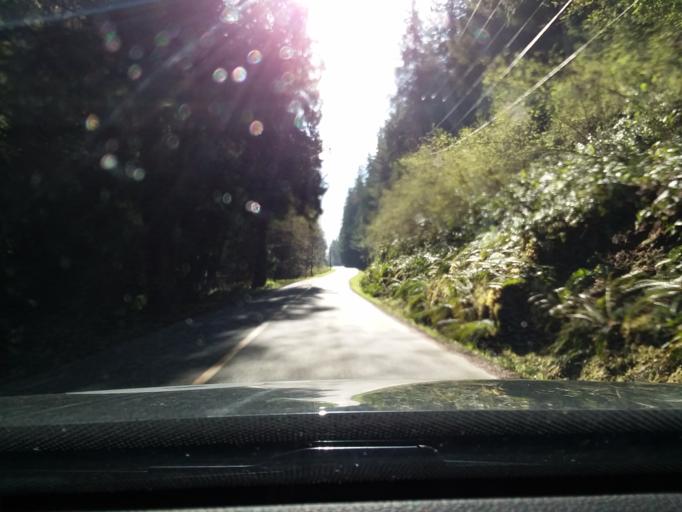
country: CA
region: British Columbia
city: North Cowichan
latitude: 48.9332
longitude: -123.4743
